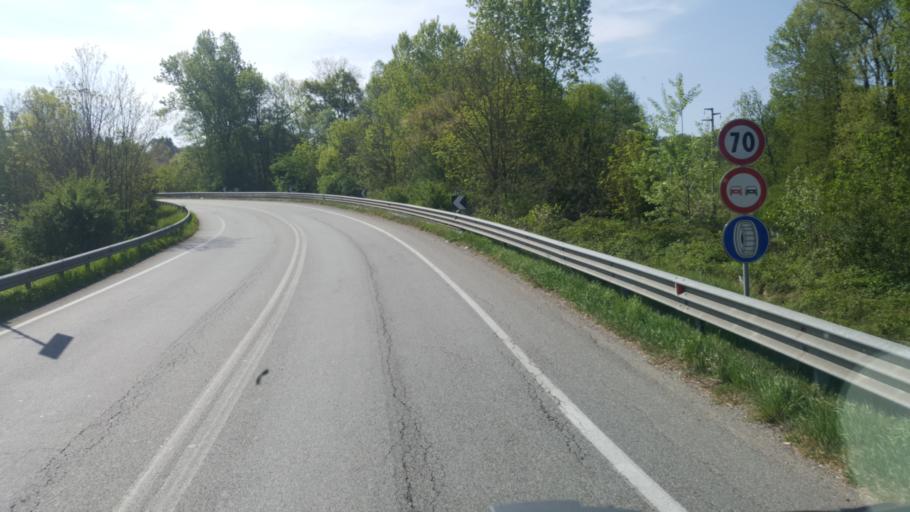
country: IT
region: Lombardy
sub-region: Provincia di Varese
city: Buguggiate
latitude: 45.7918
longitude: 8.8008
